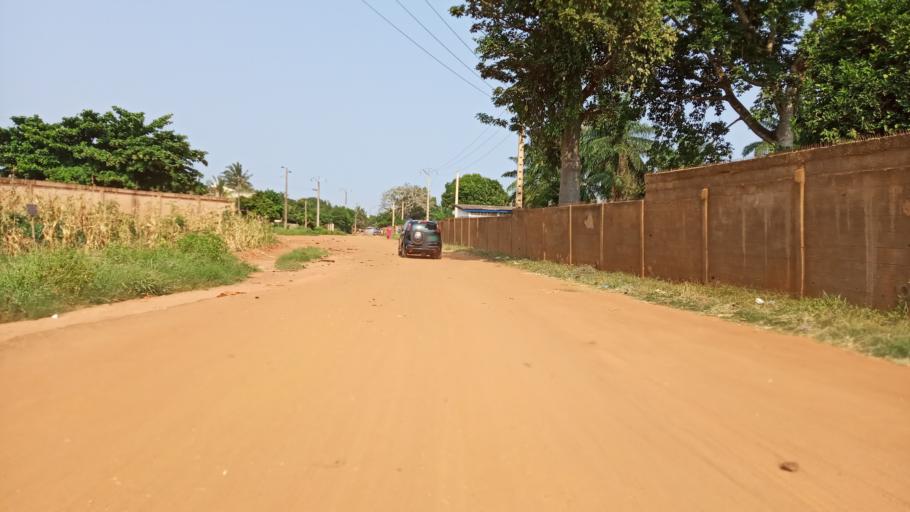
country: TG
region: Maritime
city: Lome
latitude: 6.2087
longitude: 1.2007
